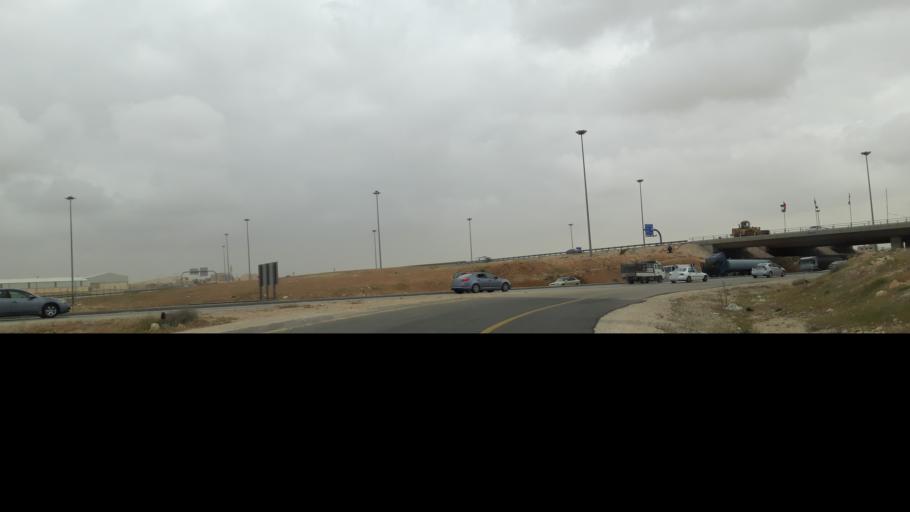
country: JO
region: Amman
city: Sahab
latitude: 31.8467
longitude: 36.0388
